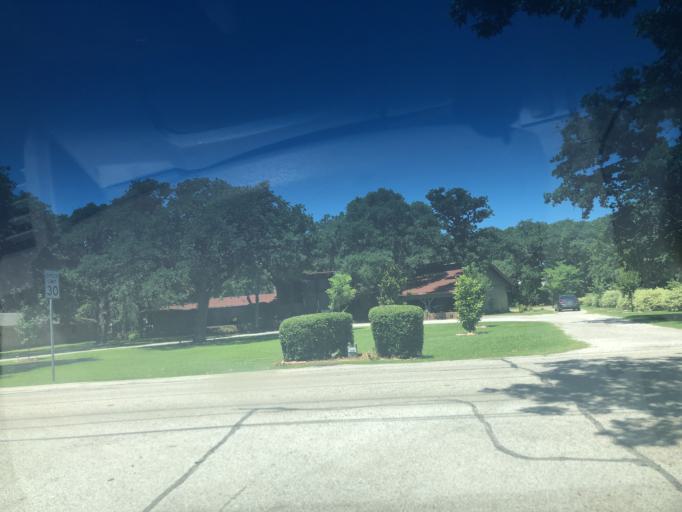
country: US
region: Texas
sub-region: Dallas County
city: Grand Prairie
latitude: 32.7787
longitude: -97.0428
